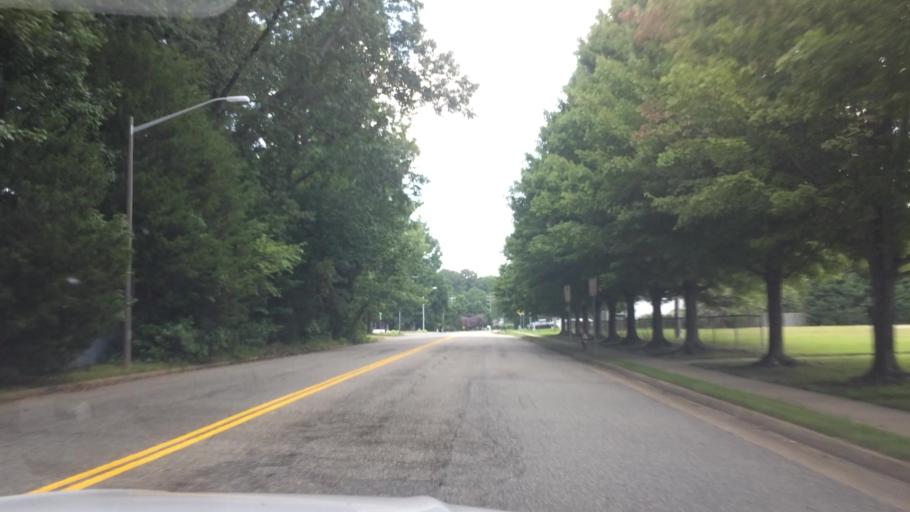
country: US
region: Virginia
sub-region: Isle of Wight County
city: Rushmere
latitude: 37.0937
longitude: -76.5353
